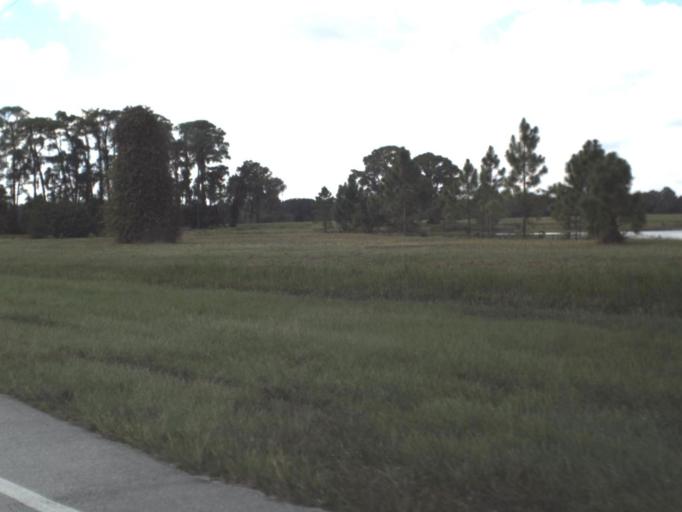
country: US
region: Florida
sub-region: Highlands County
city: Sebring
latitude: 27.4140
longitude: -81.4485
